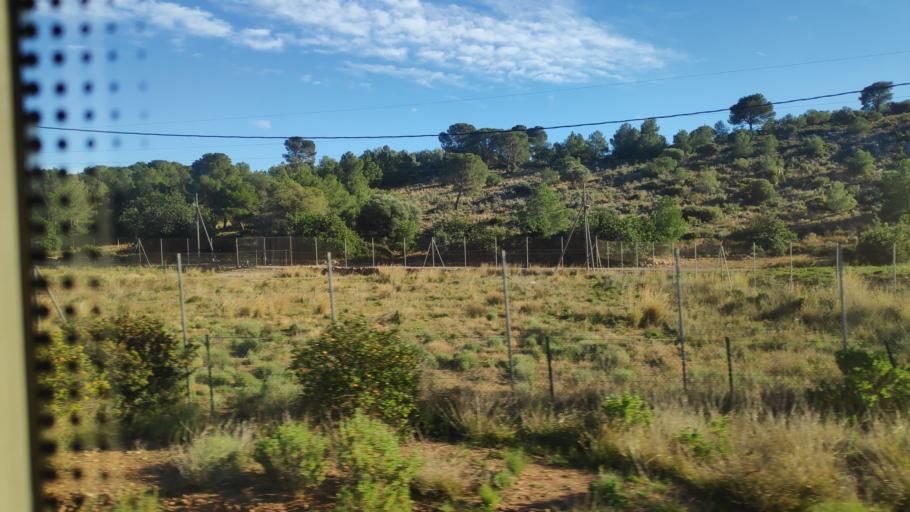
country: ES
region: Valencia
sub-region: Provincia de Castello
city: Benicassim
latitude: 40.0483
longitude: 0.0436
